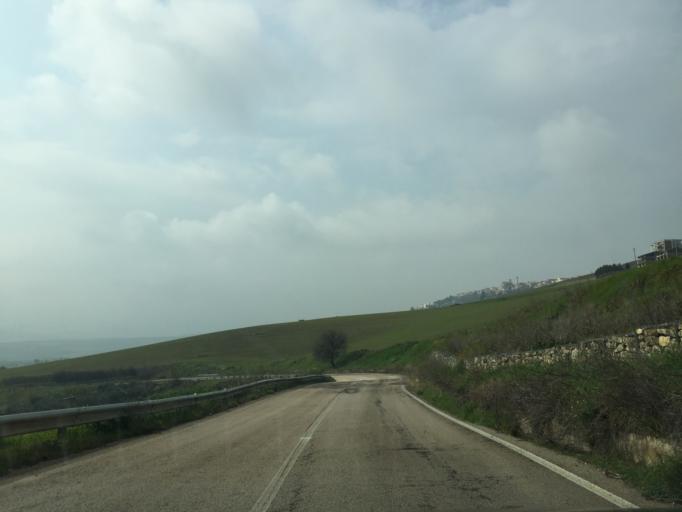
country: IT
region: Apulia
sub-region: Provincia di Foggia
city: Troia
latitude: 41.3648
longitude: 15.3251
